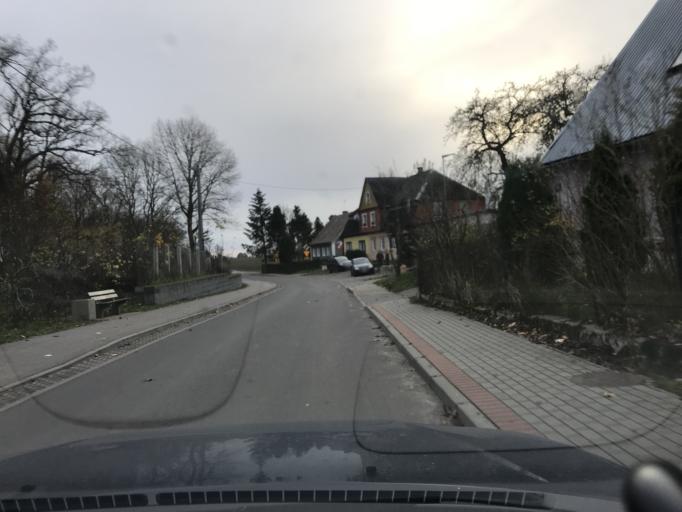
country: PL
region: Pomeranian Voivodeship
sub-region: Powiat slupski
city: Kobylnica
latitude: 54.4540
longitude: 16.8801
